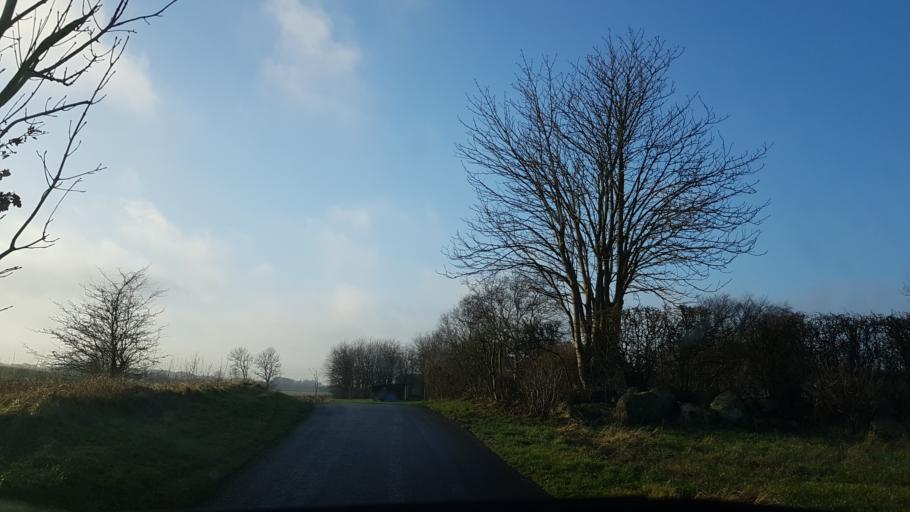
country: DK
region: South Denmark
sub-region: Aabenraa Kommune
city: Rodekro
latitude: 55.1573
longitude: 9.3092
